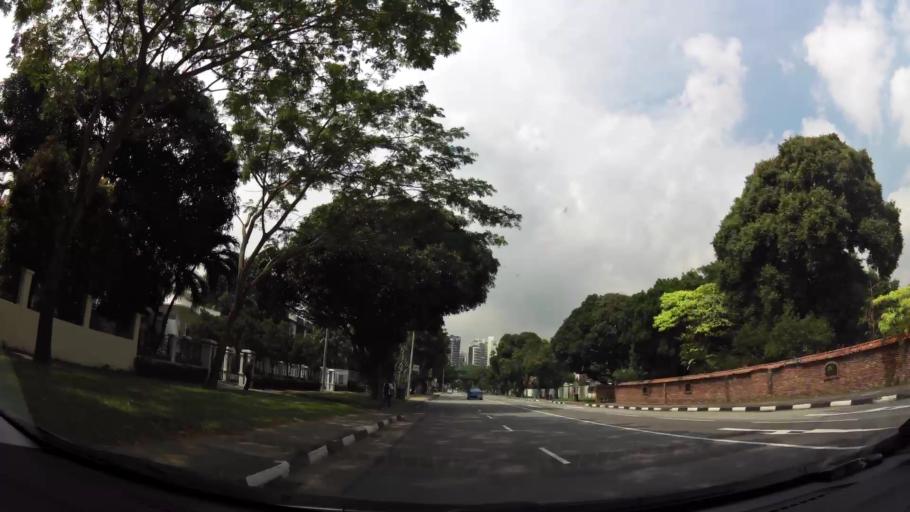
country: SG
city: Singapore
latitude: 1.3008
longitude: 103.8935
